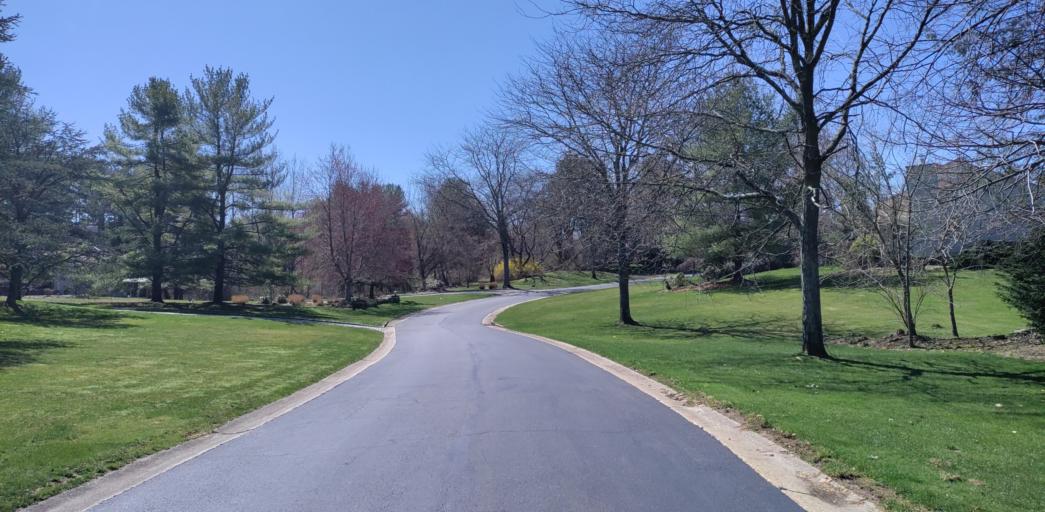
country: US
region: New York
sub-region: Nassau County
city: Old Brookville
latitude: 40.8261
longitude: -73.5956
